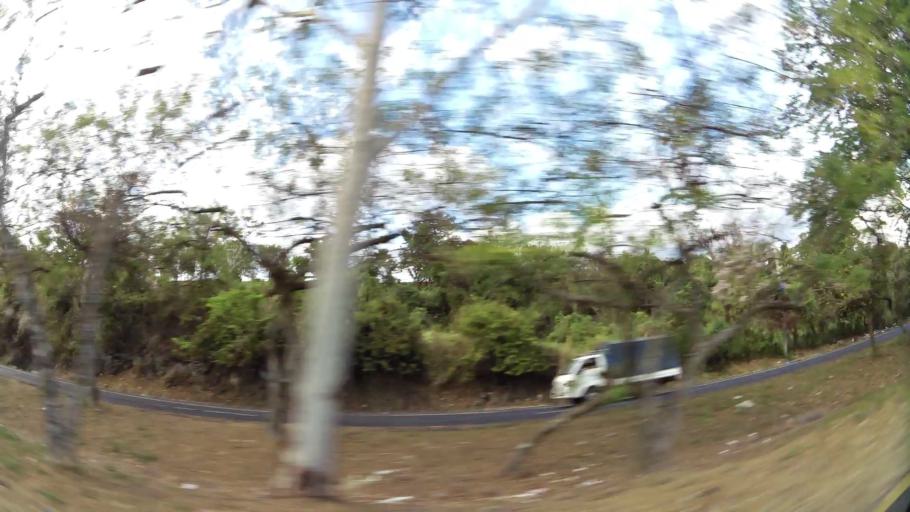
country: SV
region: San Vicente
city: San Sebastian
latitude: 13.7284
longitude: -88.8809
